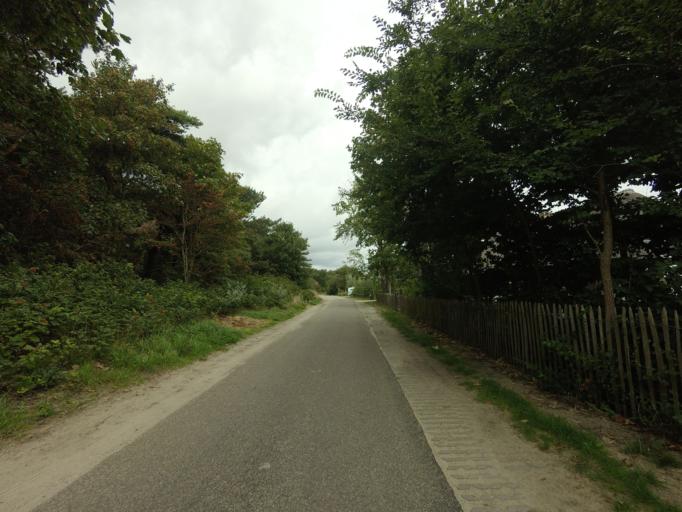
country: NL
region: Friesland
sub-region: Gemeente Ameland
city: Hollum
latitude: 53.4445
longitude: 5.6248
